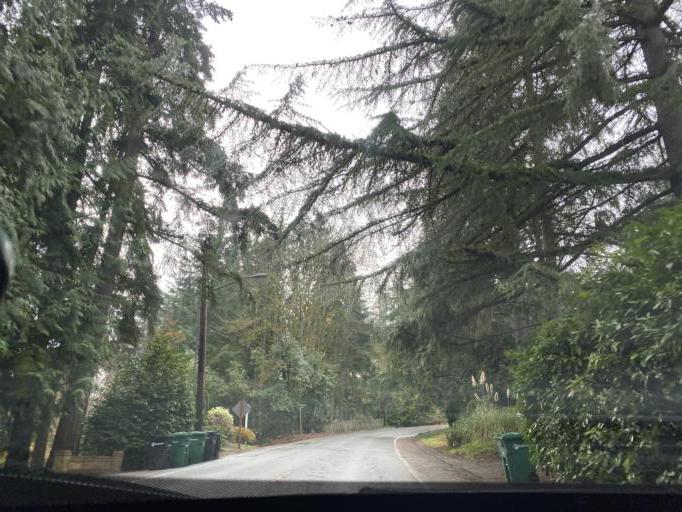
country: US
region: Washington
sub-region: King County
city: Mercer Island
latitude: 47.5398
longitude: -122.2141
